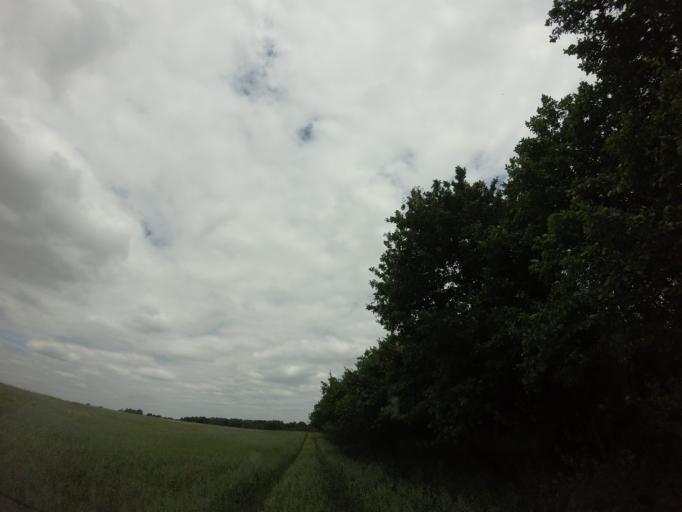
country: PL
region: West Pomeranian Voivodeship
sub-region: Powiat choszczenski
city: Krzecin
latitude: 53.0646
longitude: 15.5296
